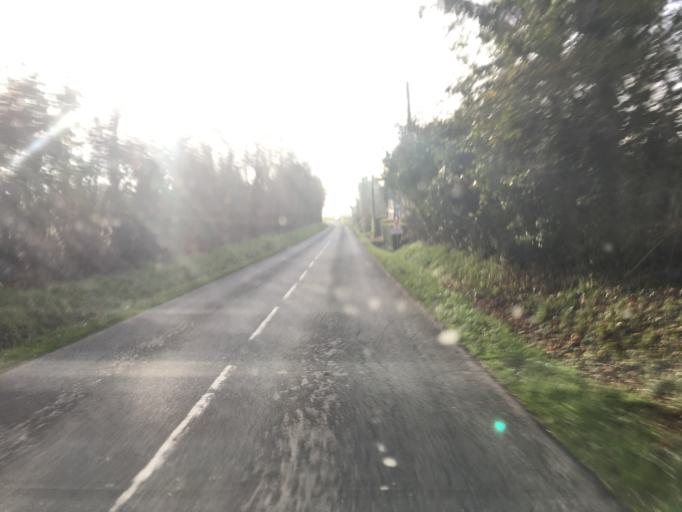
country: FR
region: Lower Normandy
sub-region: Departement du Calvados
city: Dozule
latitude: 49.2127
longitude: -0.0689
